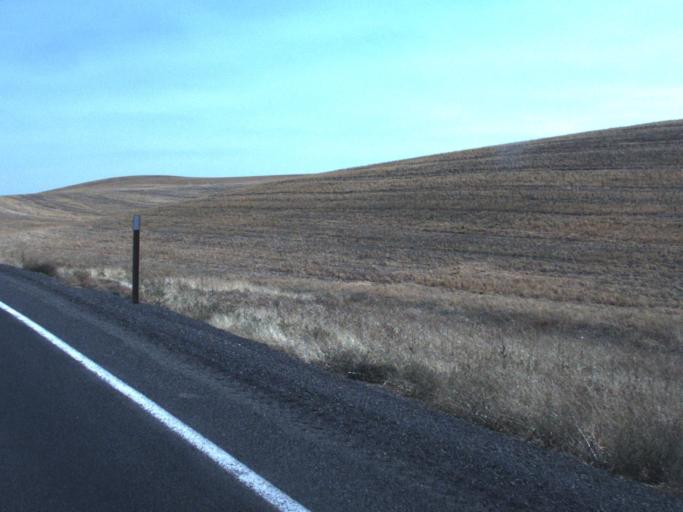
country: US
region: Idaho
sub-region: Benewah County
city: Plummer
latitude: 47.1946
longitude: -117.1028
